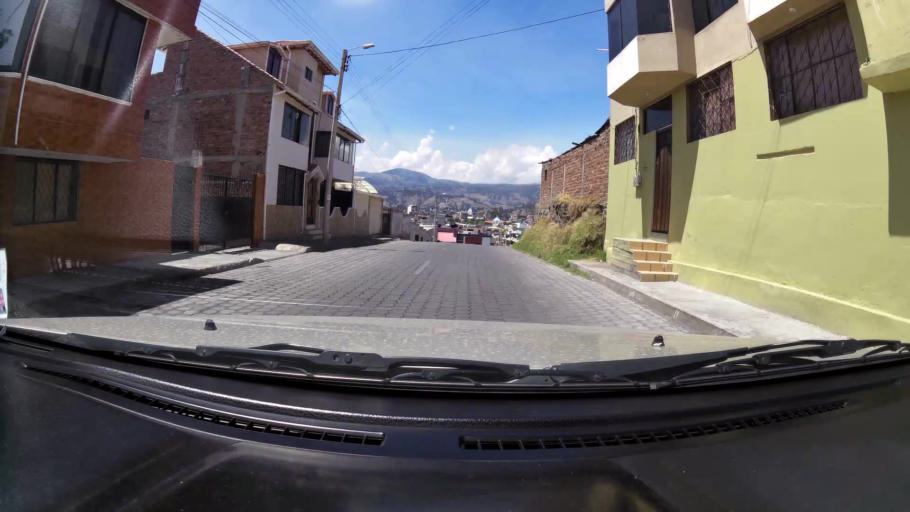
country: EC
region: Chimborazo
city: Riobamba
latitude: -1.6594
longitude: -78.6598
